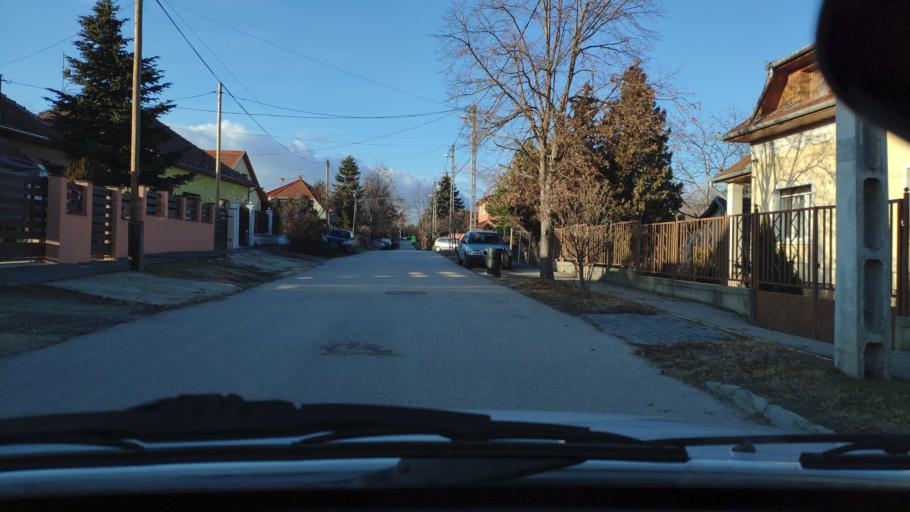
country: HU
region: Budapest
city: Budapest XXIII. keruelet
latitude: 47.3930
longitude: 19.0987
